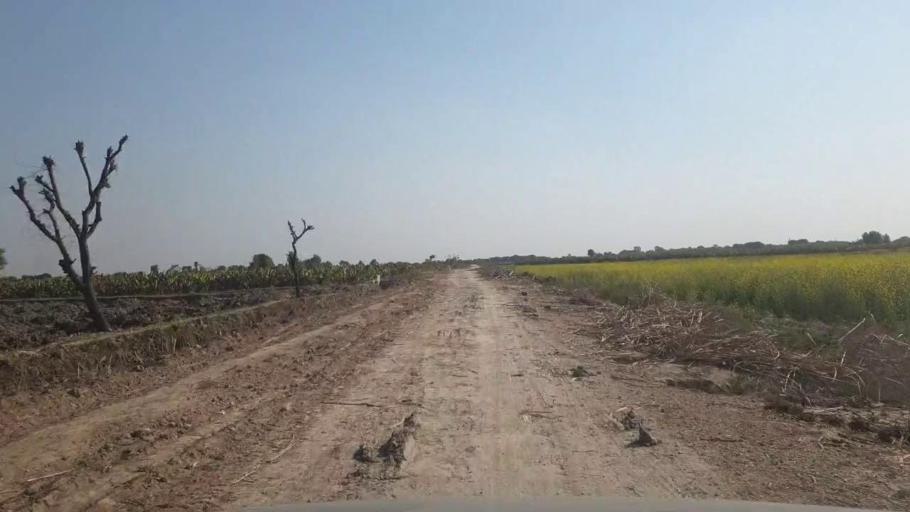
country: PK
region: Sindh
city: Chambar
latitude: 25.3169
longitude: 68.8718
